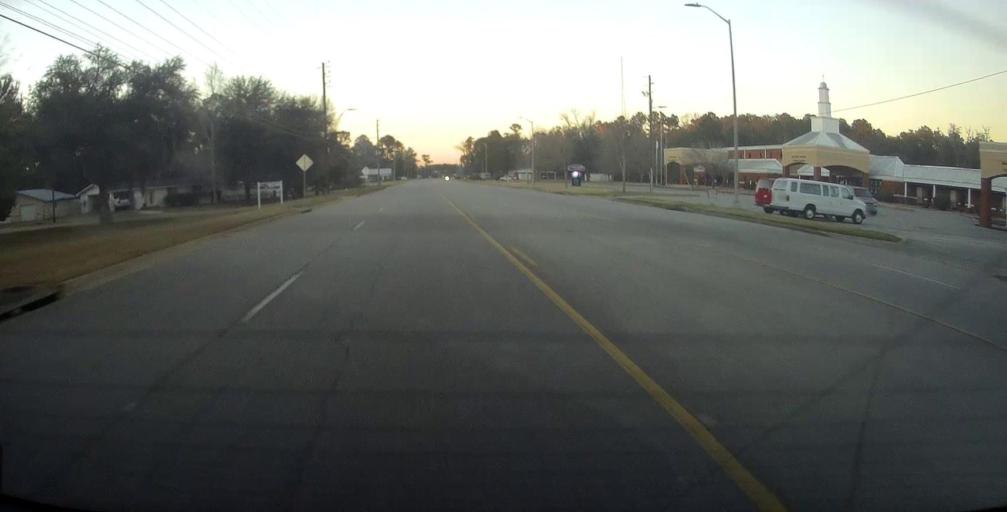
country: US
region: Georgia
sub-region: Dougherty County
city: Albany
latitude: 31.5429
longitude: -84.1366
